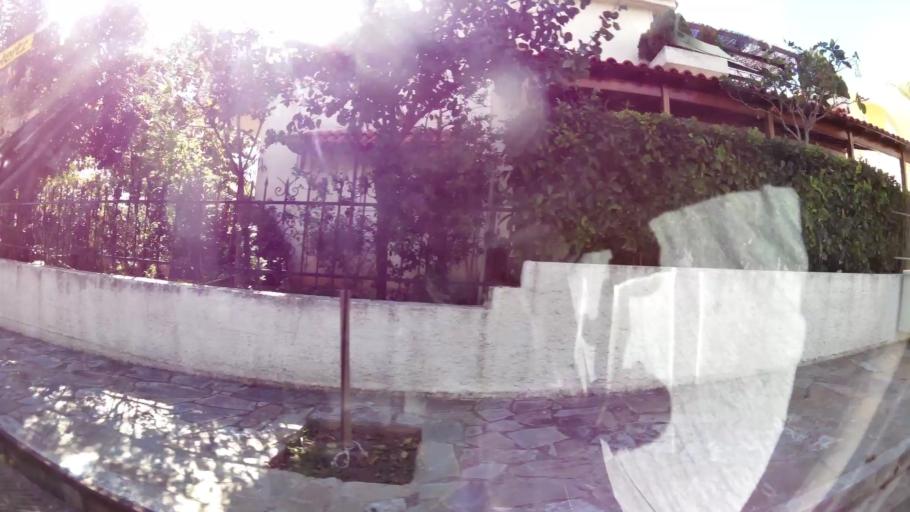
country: GR
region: Attica
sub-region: Nomarchia Anatolikis Attikis
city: Voula
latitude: 37.8397
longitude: 23.7852
